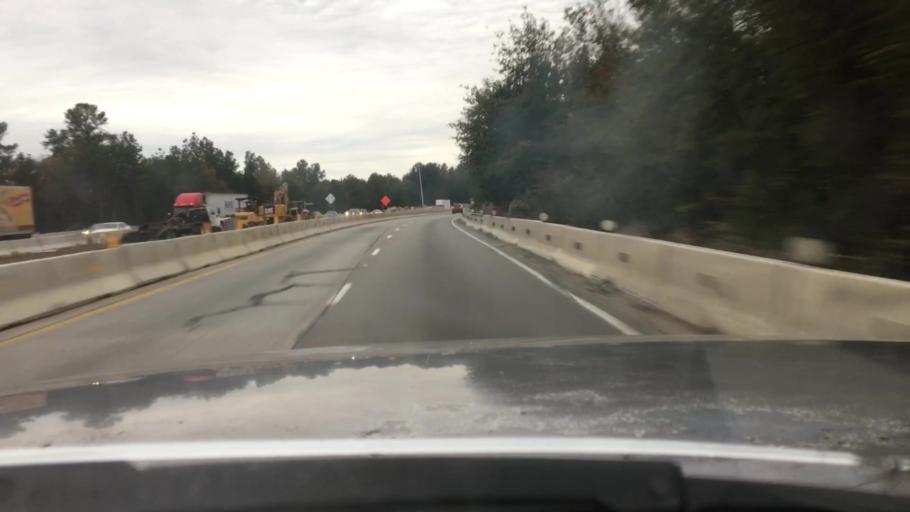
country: US
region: South Carolina
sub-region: Lexington County
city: Lexington
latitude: 33.9723
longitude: -81.1977
